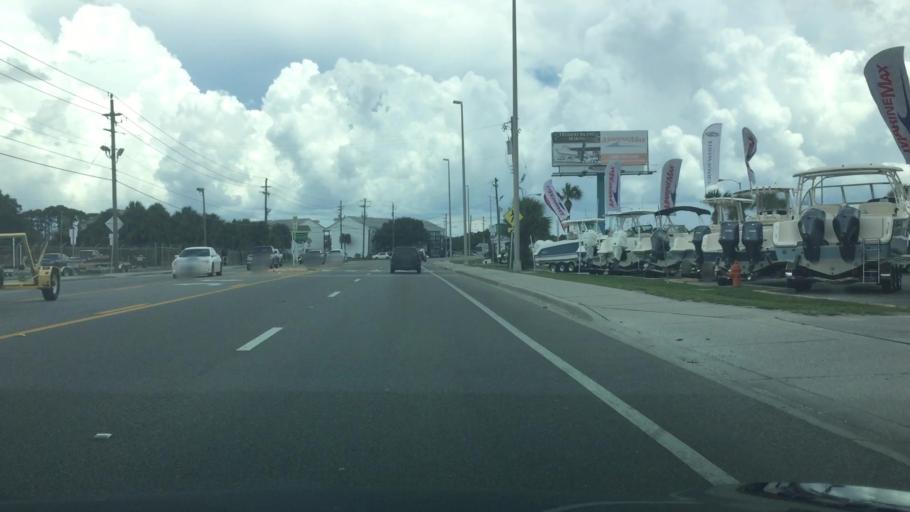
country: US
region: Florida
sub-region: Bay County
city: Lower Grand Lagoon
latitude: 30.1439
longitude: -85.7495
